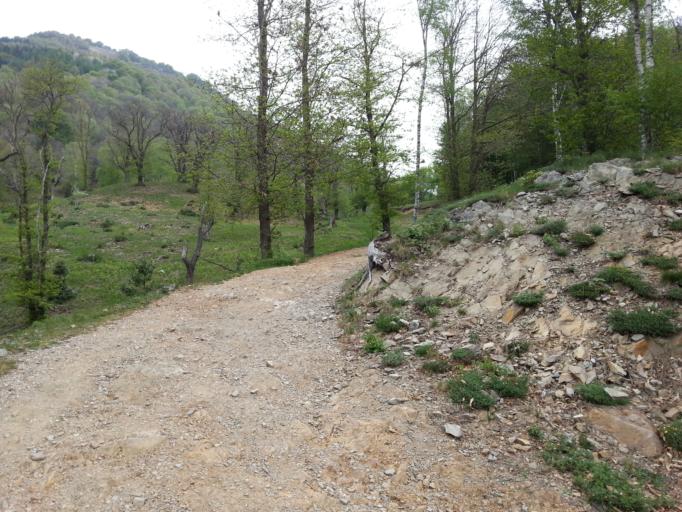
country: CH
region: Ticino
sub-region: Lugano District
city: Bioggio
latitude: 46.0387
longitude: 8.8707
